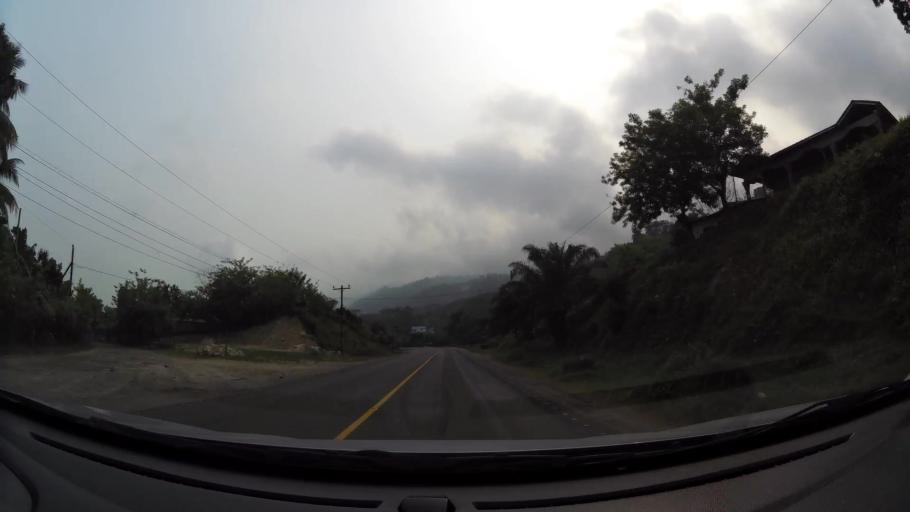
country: HN
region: Yoro
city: Toyos
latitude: 15.5607
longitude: -87.6215
